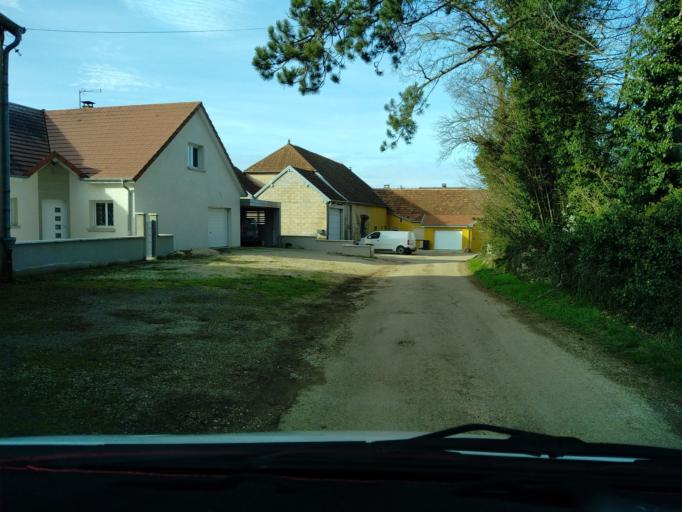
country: FR
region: Franche-Comte
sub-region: Departement de la Haute-Saone
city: Marnay
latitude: 47.3632
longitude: 5.7164
